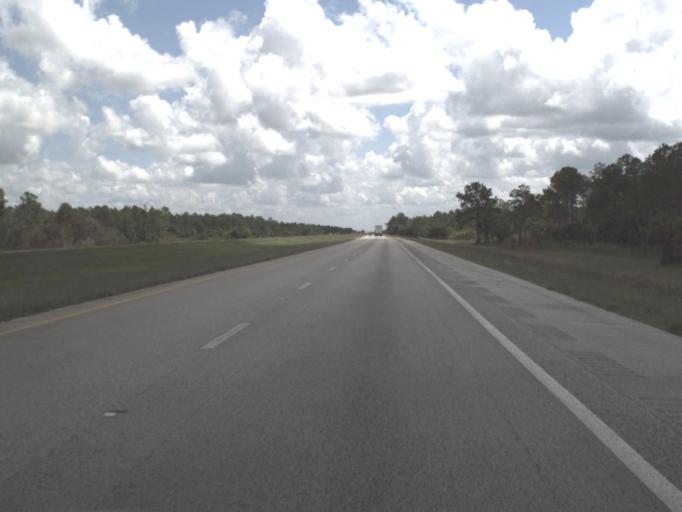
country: US
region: Florida
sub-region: Collier County
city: Golden Gate
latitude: 26.1532
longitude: -81.5900
